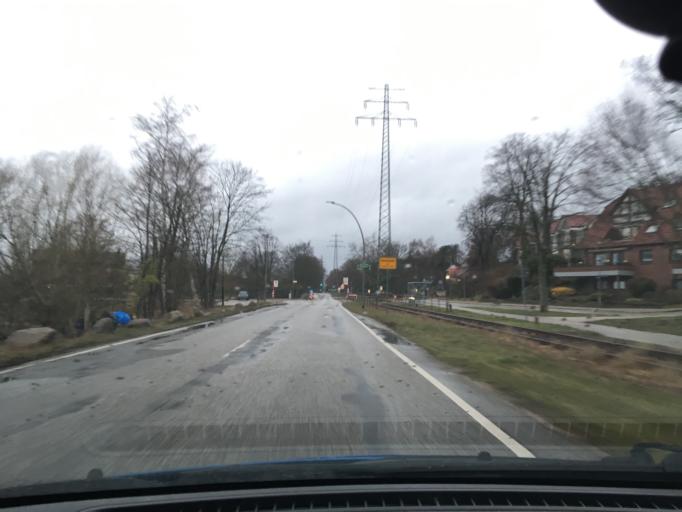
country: DE
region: Schleswig-Holstein
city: Geesthacht
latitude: 53.4260
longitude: 10.3787
